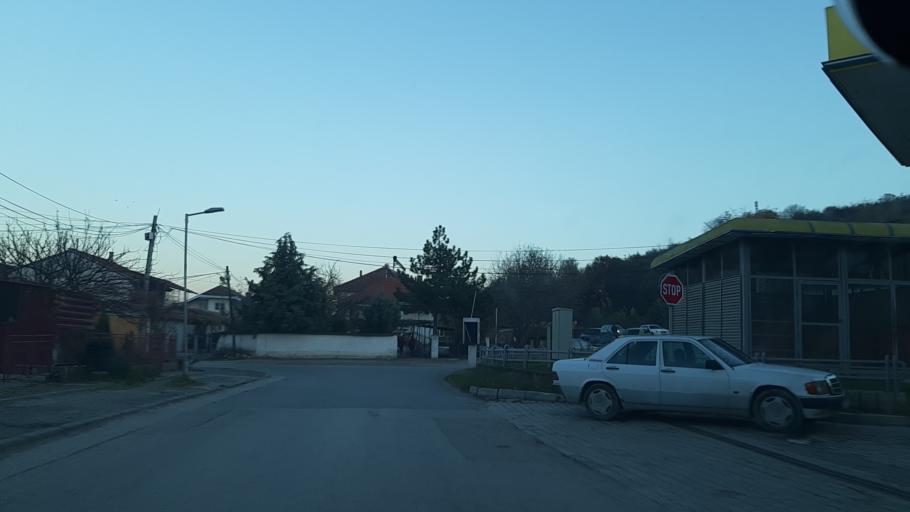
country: MK
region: Kisela Voda
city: Kisela Voda
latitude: 41.9363
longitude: 21.5132
